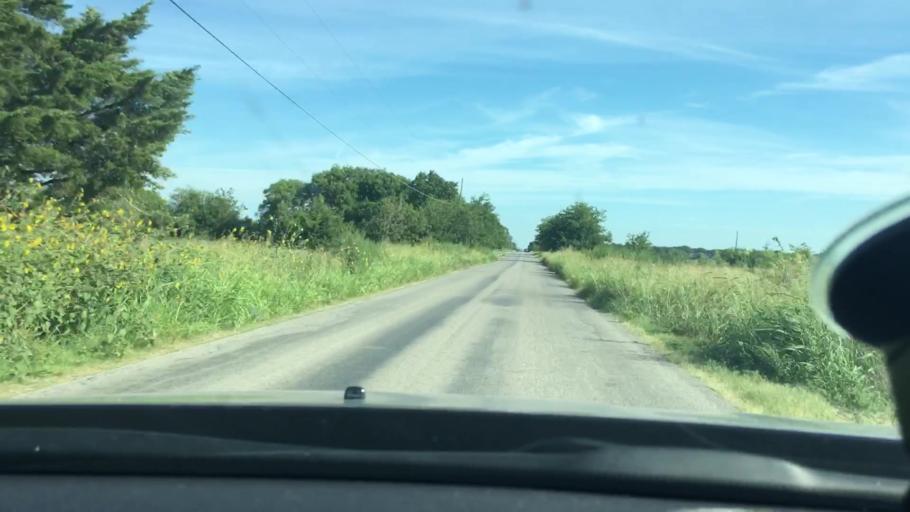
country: US
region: Oklahoma
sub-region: Carter County
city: Lone Grove
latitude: 34.1971
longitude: -97.2475
